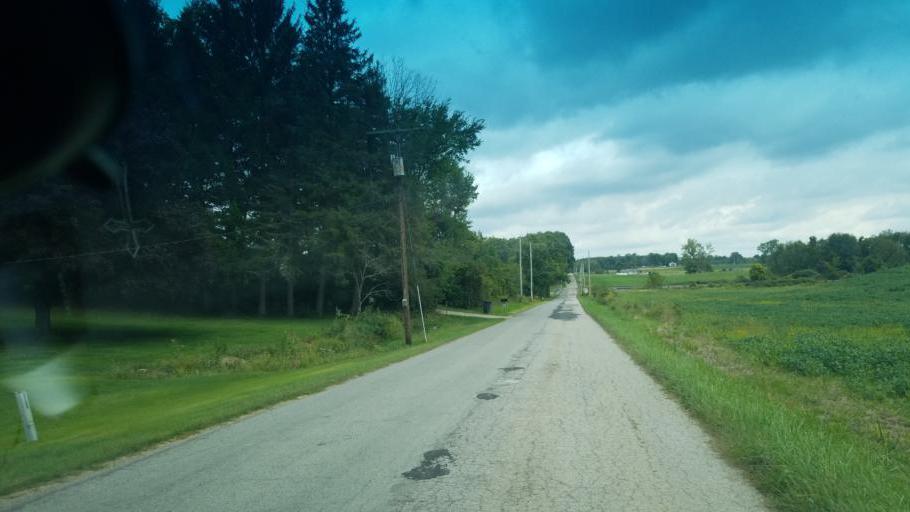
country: US
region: Ohio
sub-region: Richland County
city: Ontario
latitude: 40.8059
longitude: -82.5709
